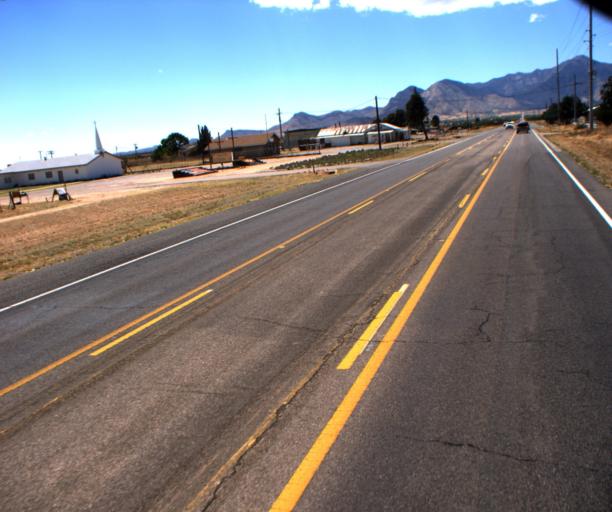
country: US
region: Arizona
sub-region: Cochise County
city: Sierra Vista Southeast
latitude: 31.3800
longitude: -110.1205
